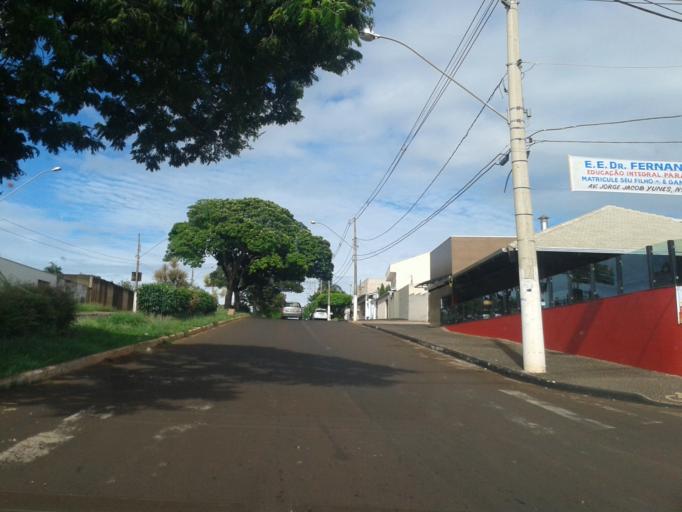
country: BR
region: Minas Gerais
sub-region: Ituiutaba
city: Ituiutaba
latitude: -18.9649
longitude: -49.4639
